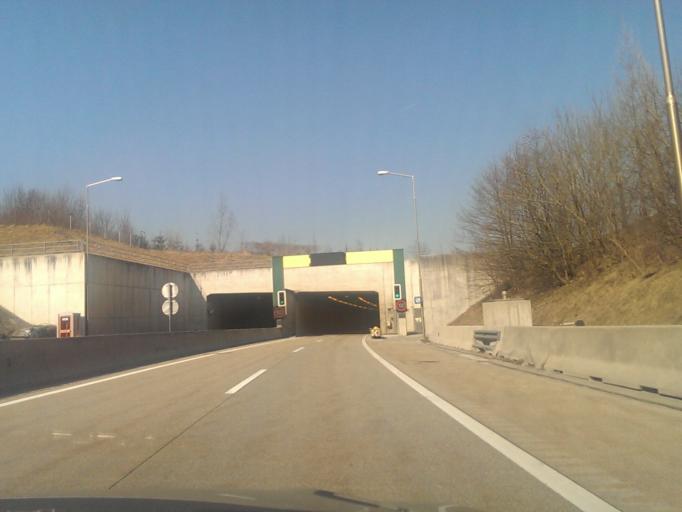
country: AT
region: Upper Austria
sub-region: Politischer Bezirk Kirchdorf an der Krems
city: Micheldorf in Oberoesterreich
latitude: 47.8743
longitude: 14.1152
